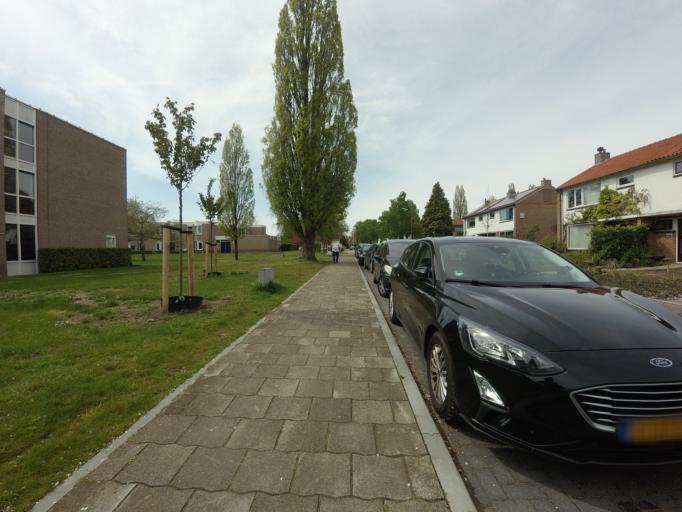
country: NL
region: Utrecht
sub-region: Gemeente Utrechtse Heuvelrug
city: Amerongen
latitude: 52.0004
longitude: 5.4666
